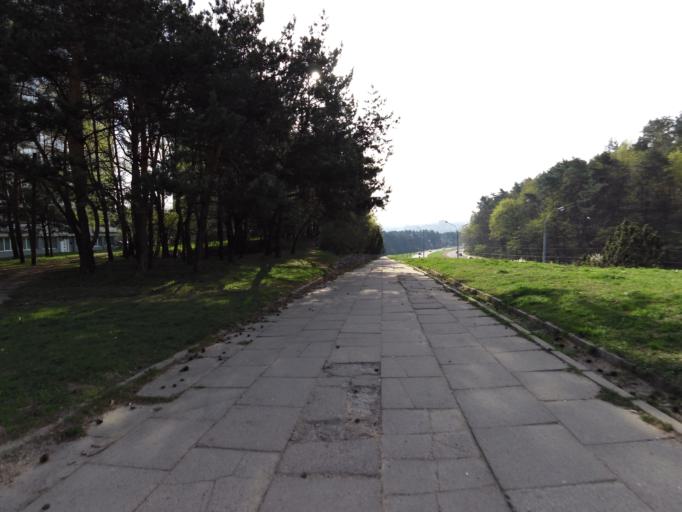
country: LT
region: Vilnius County
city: Lazdynai
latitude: 54.6786
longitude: 25.2171
